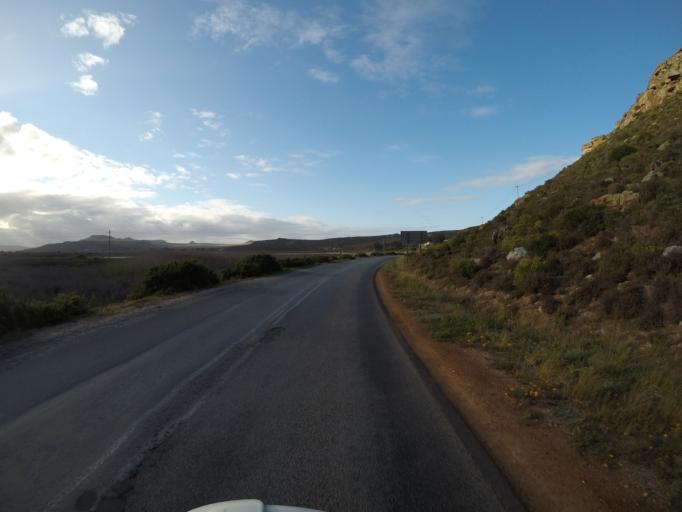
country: ZA
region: Western Cape
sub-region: West Coast District Municipality
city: Clanwilliam
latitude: -32.3169
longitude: 18.3576
